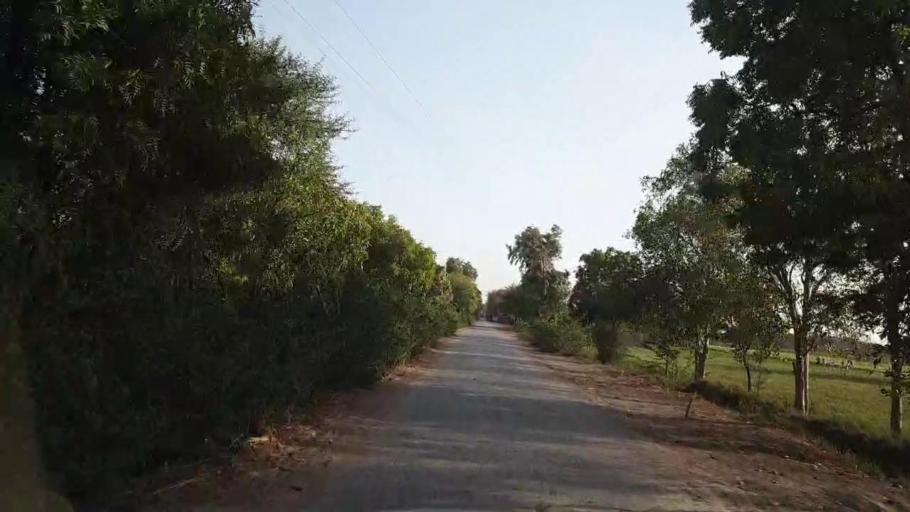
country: PK
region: Sindh
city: Tando Ghulam Ali
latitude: 25.1234
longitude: 68.9069
